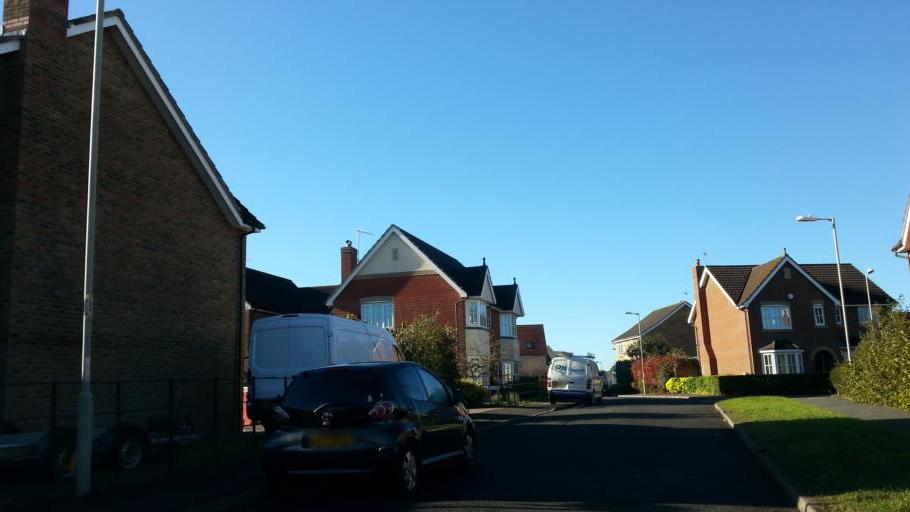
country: GB
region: England
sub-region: Suffolk
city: Kesgrave
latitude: 52.0597
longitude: 1.2590
